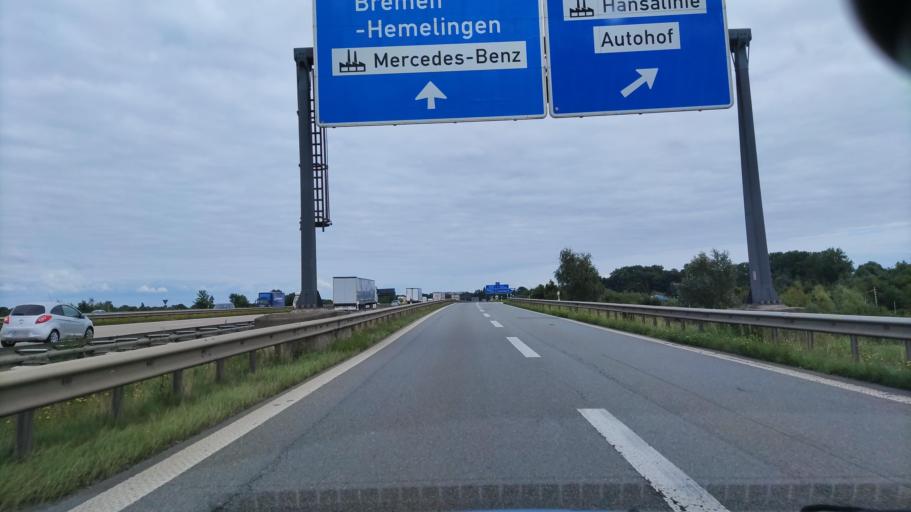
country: DE
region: Bremen
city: Bremen
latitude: 53.0368
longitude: 8.8809
